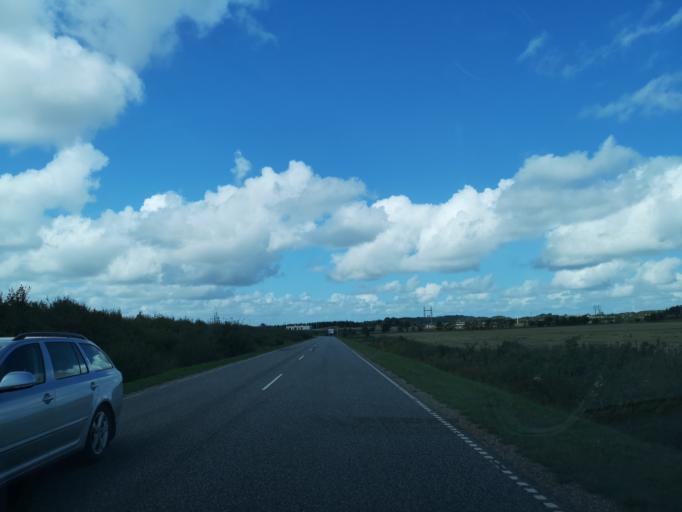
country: DK
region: Central Jutland
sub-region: Holstebro Kommune
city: Holstebro
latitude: 56.3907
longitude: 8.5907
